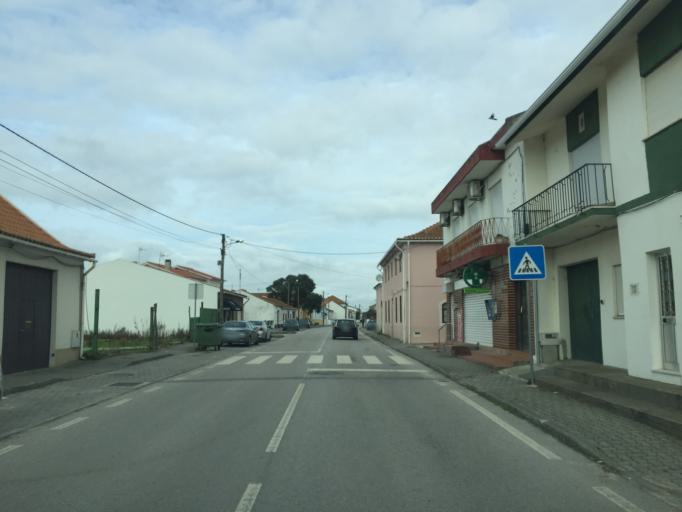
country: PT
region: Coimbra
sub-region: Figueira da Foz
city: Lavos
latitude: 40.0290
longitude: -8.8211
